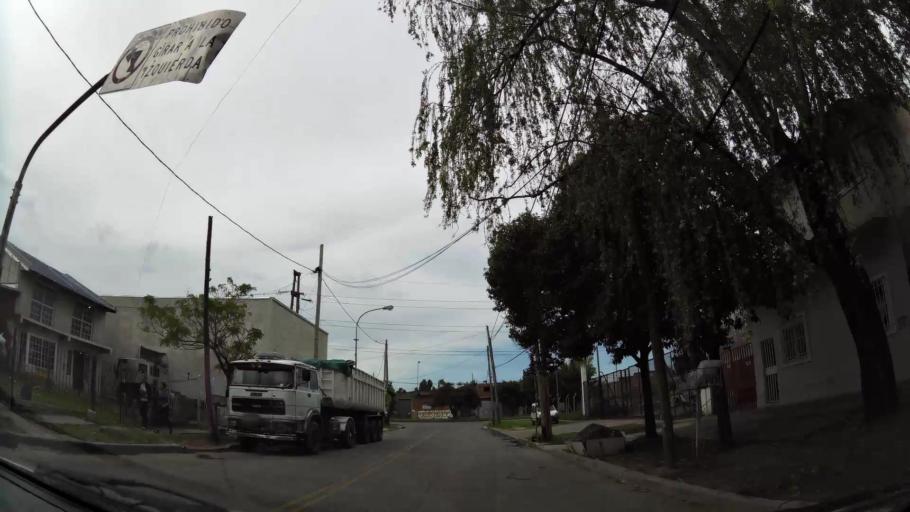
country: AR
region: Buenos Aires
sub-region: Partido de Quilmes
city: Quilmes
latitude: -34.7535
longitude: -58.2615
